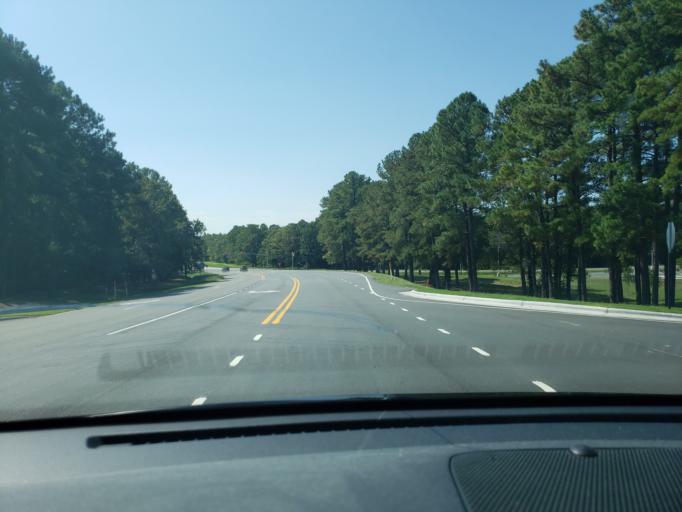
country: US
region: North Carolina
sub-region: Wake County
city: Morrisville
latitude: 35.9009
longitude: -78.8800
